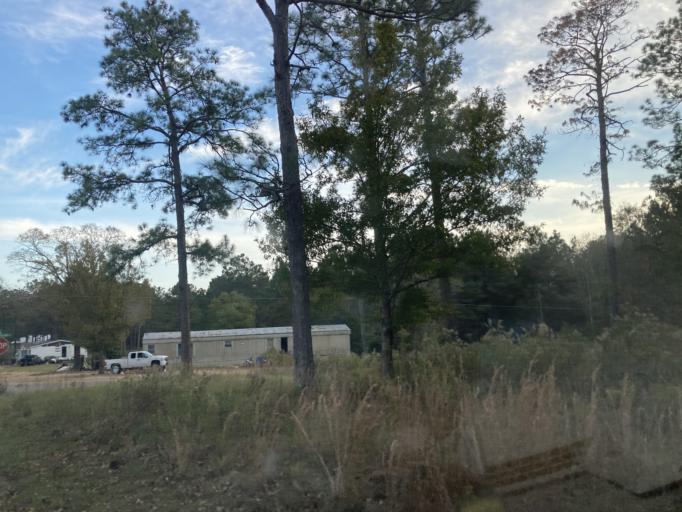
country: US
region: Mississippi
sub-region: Lamar County
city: Purvis
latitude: 31.1842
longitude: -89.3523
